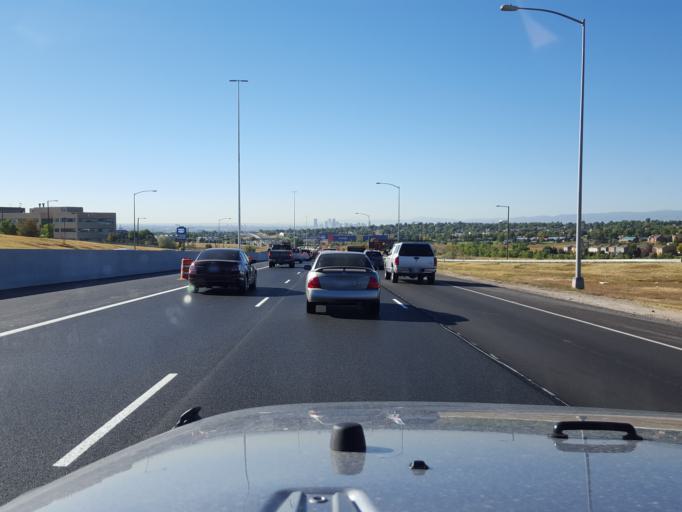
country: US
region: Colorado
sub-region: Adams County
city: Thornton
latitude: 39.8670
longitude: -104.9877
